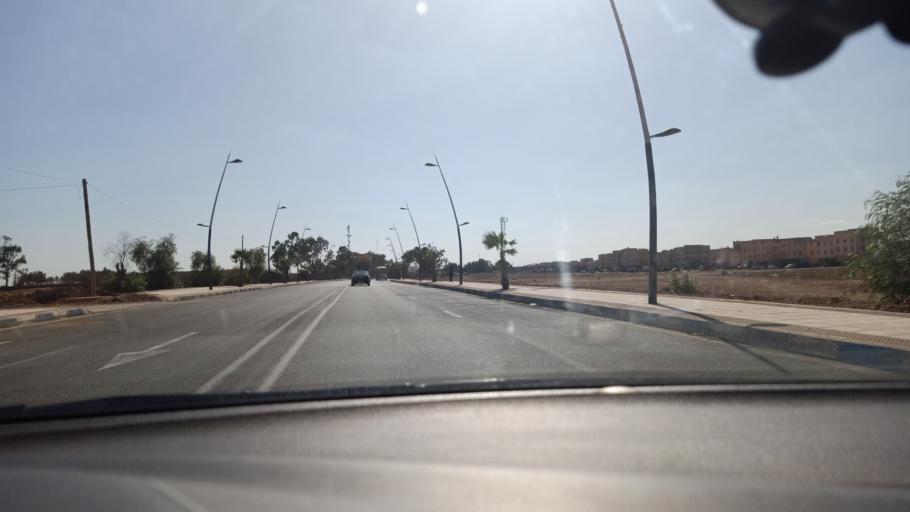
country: MA
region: Doukkala-Abda
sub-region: Safi
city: Youssoufia
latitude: 32.0853
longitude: -8.6196
